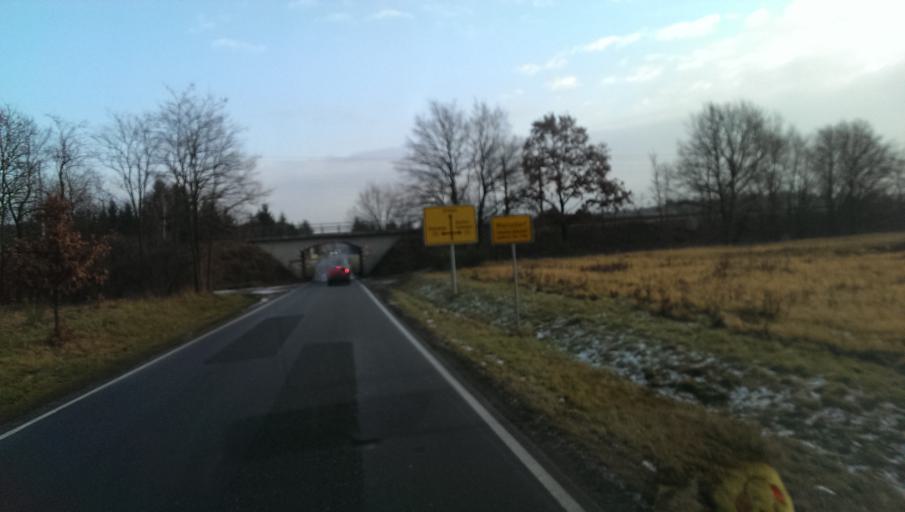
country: DE
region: Brandenburg
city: Merzdorf
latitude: 51.4102
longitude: 13.4936
